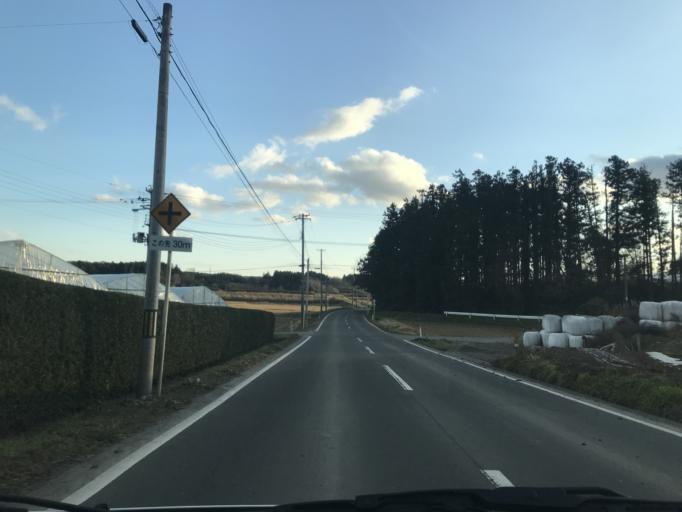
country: JP
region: Miyagi
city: Kogota
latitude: 38.6348
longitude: 141.0696
